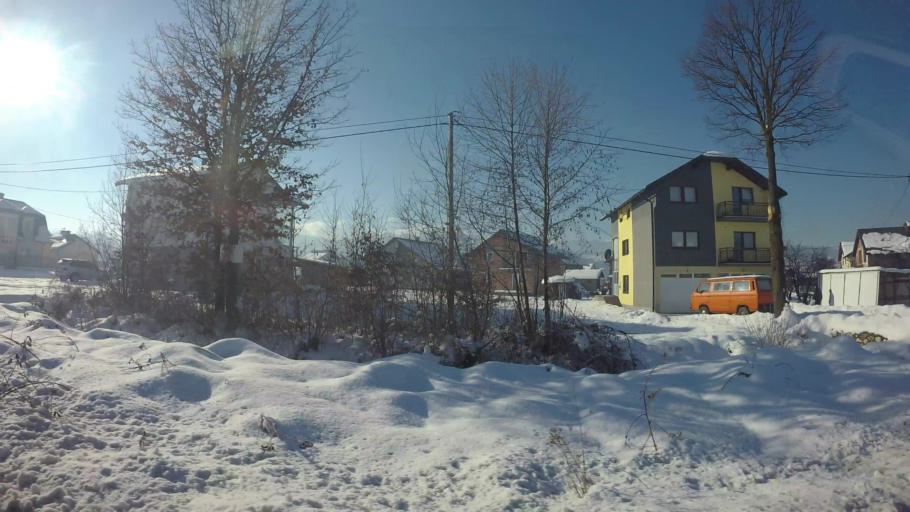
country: BA
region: Federation of Bosnia and Herzegovina
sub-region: Kanton Sarajevo
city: Sarajevo
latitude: 43.8210
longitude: 18.3797
